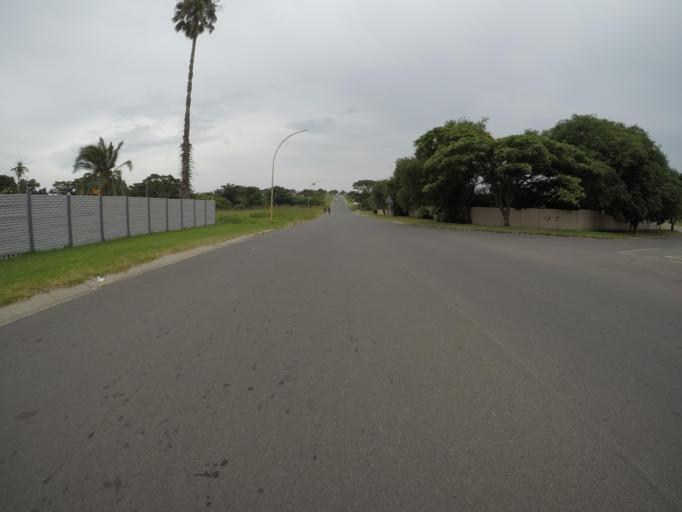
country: ZA
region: Eastern Cape
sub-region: Buffalo City Metropolitan Municipality
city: East London
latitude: -33.0024
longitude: 27.8575
